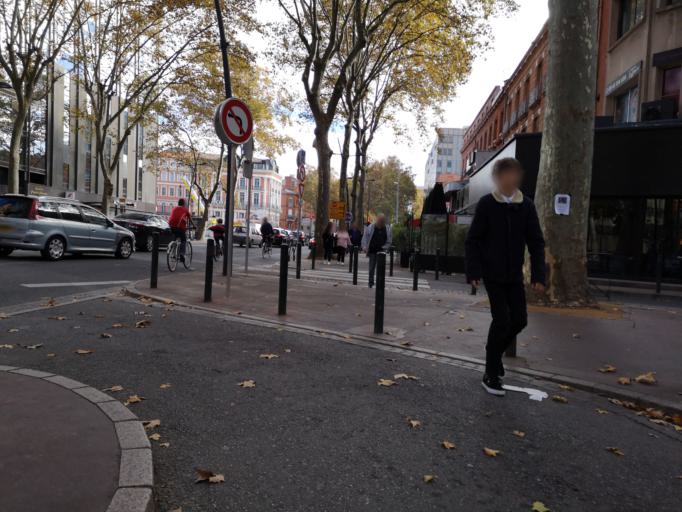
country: FR
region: Midi-Pyrenees
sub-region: Departement de la Haute-Garonne
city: Toulouse
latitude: 43.6065
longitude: 1.4477
